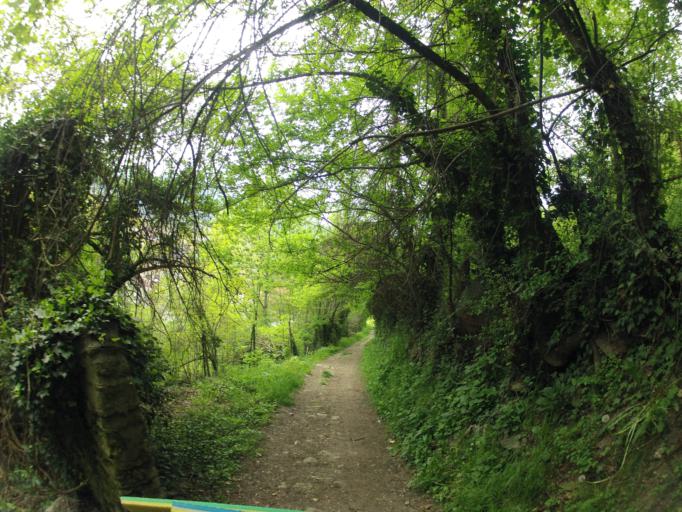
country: IT
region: Piedmont
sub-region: Provincia di Cuneo
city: Peveragno
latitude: 44.3322
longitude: 7.6148
